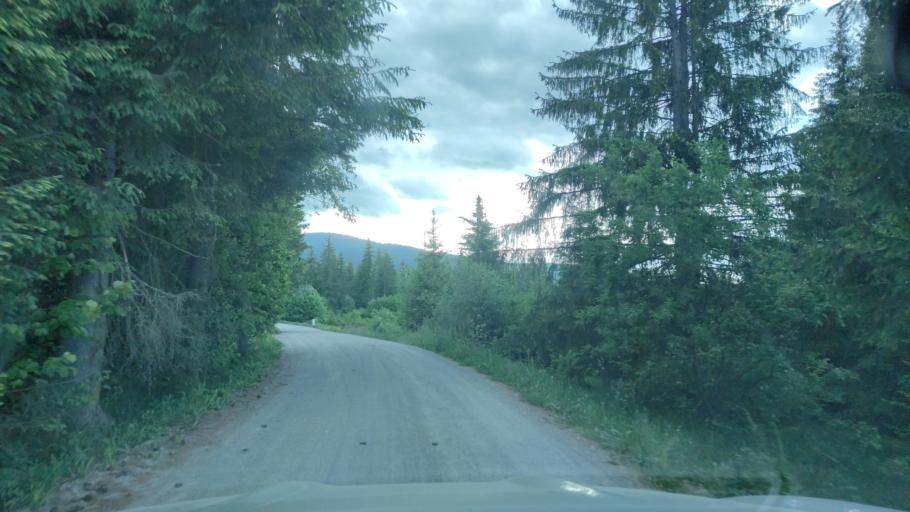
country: RO
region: Harghita
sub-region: Comuna Joseni
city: Joseni
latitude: 46.6667
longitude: 25.3818
